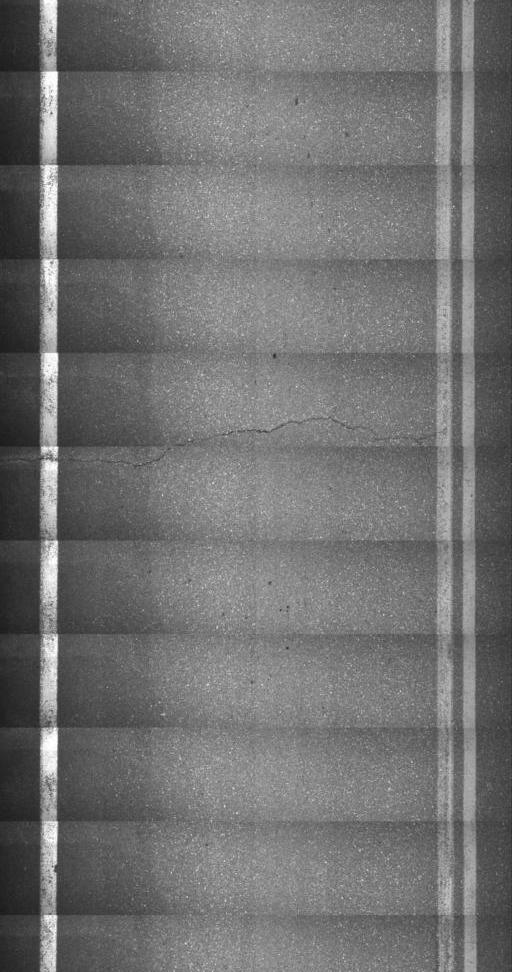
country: US
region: Vermont
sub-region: Orleans County
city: Newport
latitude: 44.7706
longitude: -72.0543
